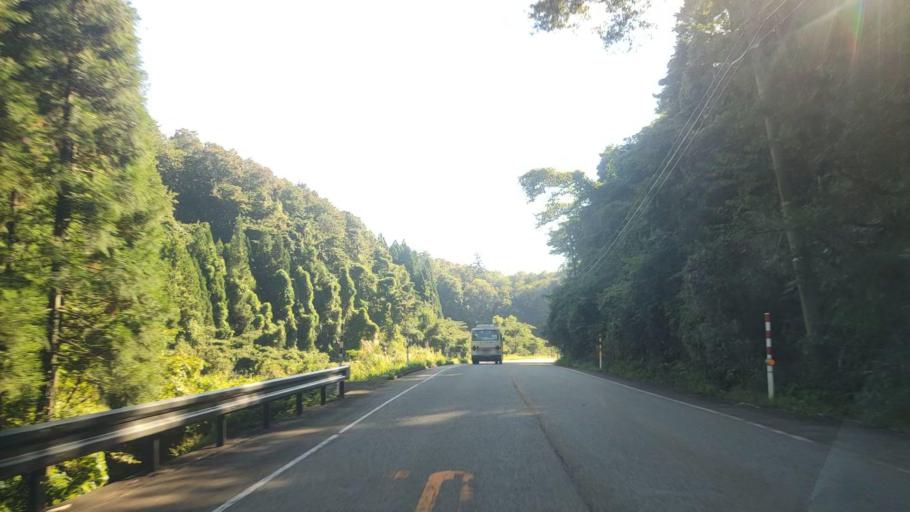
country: JP
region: Ishikawa
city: Nanao
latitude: 37.2480
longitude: 136.9943
